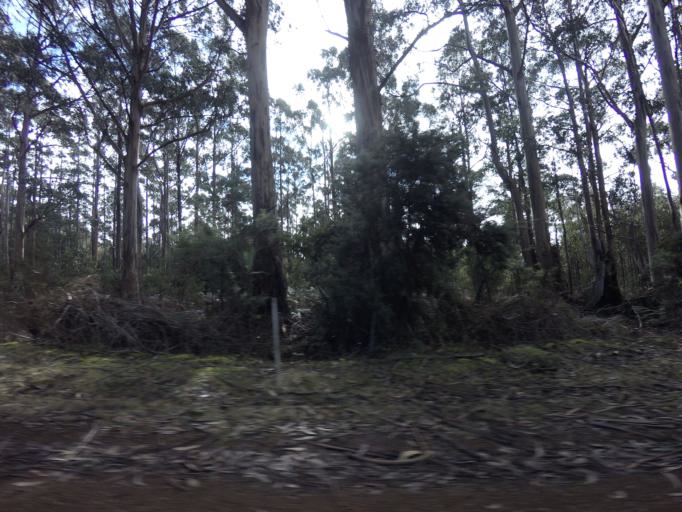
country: AU
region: Tasmania
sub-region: Derwent Valley
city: New Norfolk
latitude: -42.7859
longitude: 146.9157
